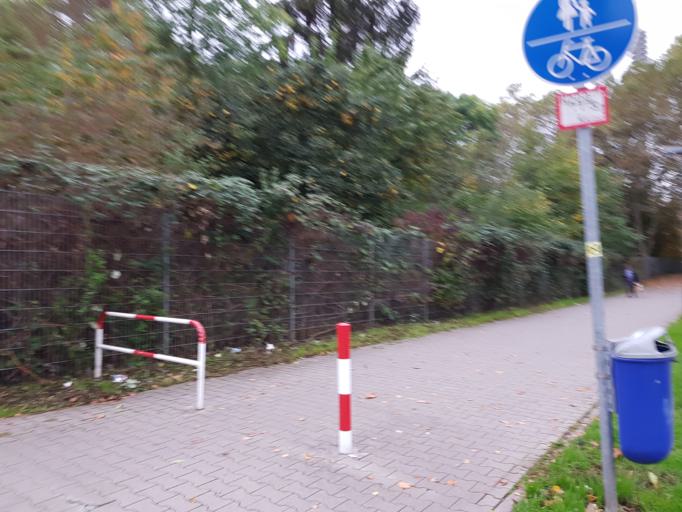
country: DE
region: Hesse
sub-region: Regierungsbezirk Darmstadt
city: Frankfurt am Main
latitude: 50.1410
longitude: 8.6604
